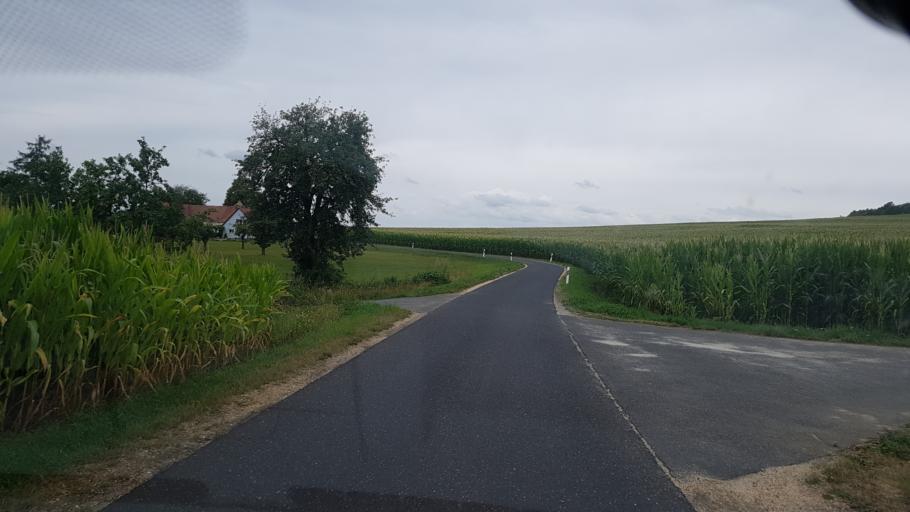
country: DE
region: Saxony
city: Kodersdorf
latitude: 51.2250
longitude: 14.8774
